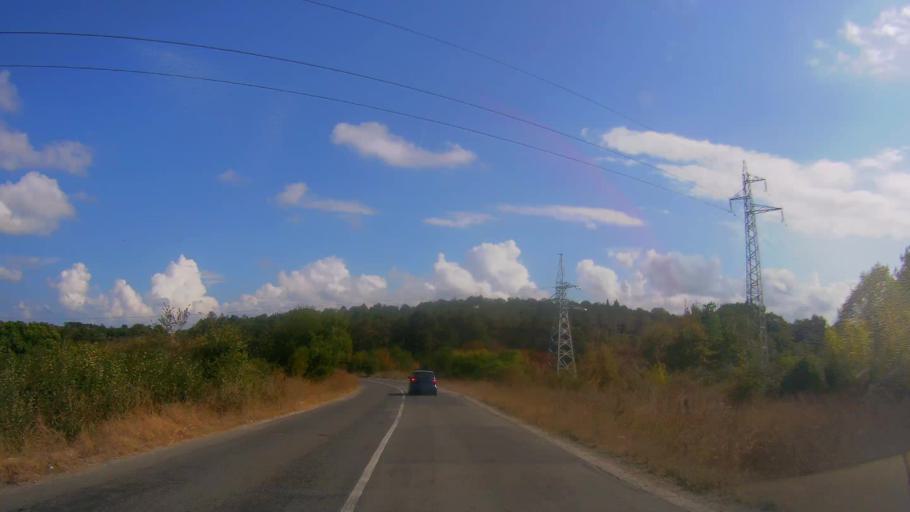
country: BG
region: Burgas
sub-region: Obshtina Burgas
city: Burgas
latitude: 42.4750
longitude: 27.3968
